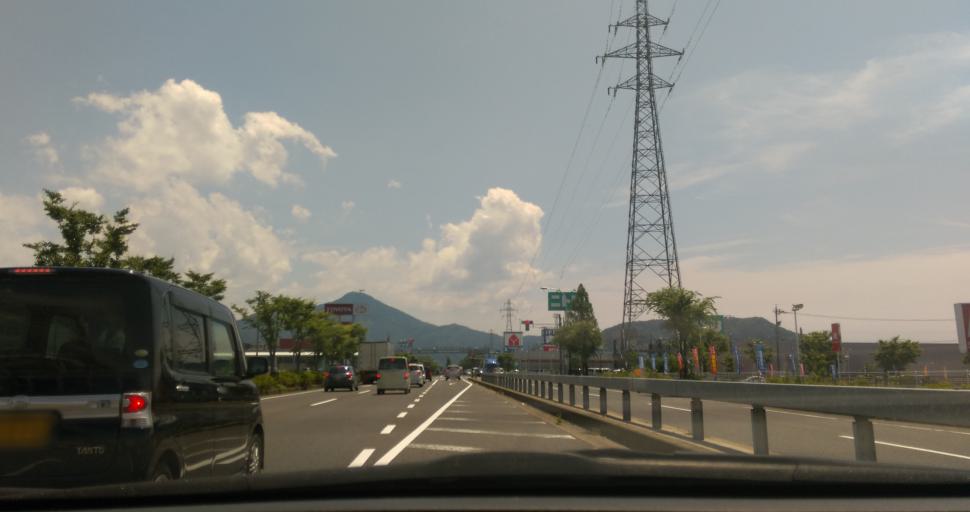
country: JP
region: Fukui
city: Sabae
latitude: 35.9276
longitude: 136.1902
